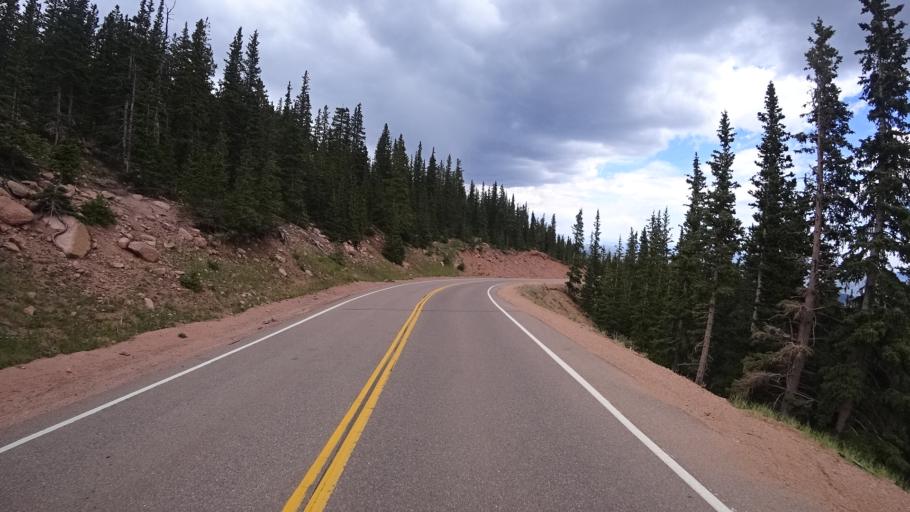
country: US
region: Colorado
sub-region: El Paso County
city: Cascade-Chipita Park
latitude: 38.8773
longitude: -105.0734
